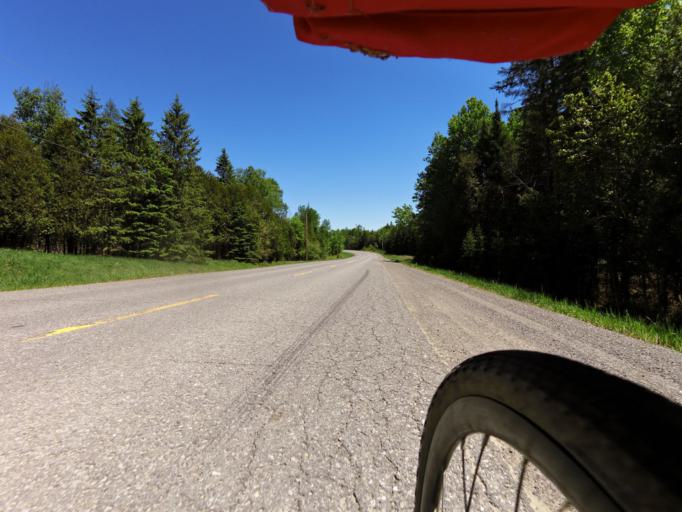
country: CA
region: Ontario
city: Carleton Place
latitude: 45.1836
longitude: -76.3884
